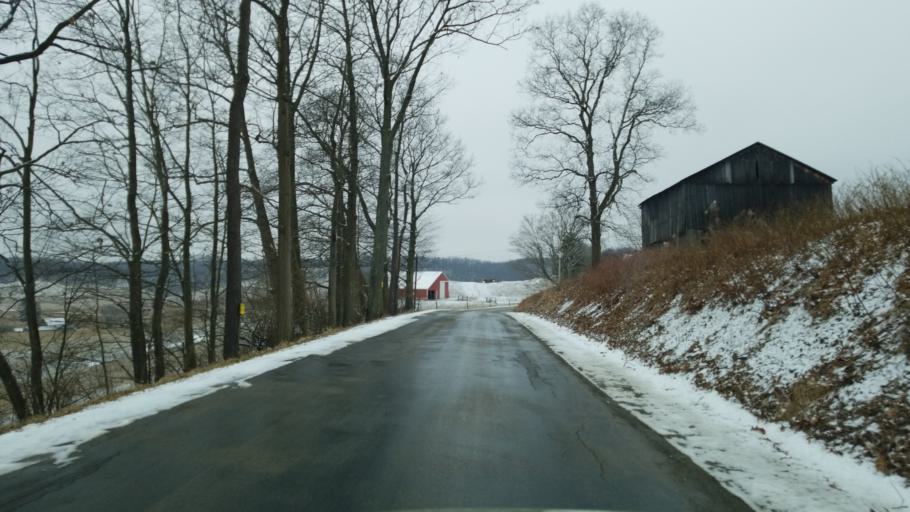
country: US
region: Pennsylvania
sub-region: Jefferson County
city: Sykesville
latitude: 41.0830
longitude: -78.8140
